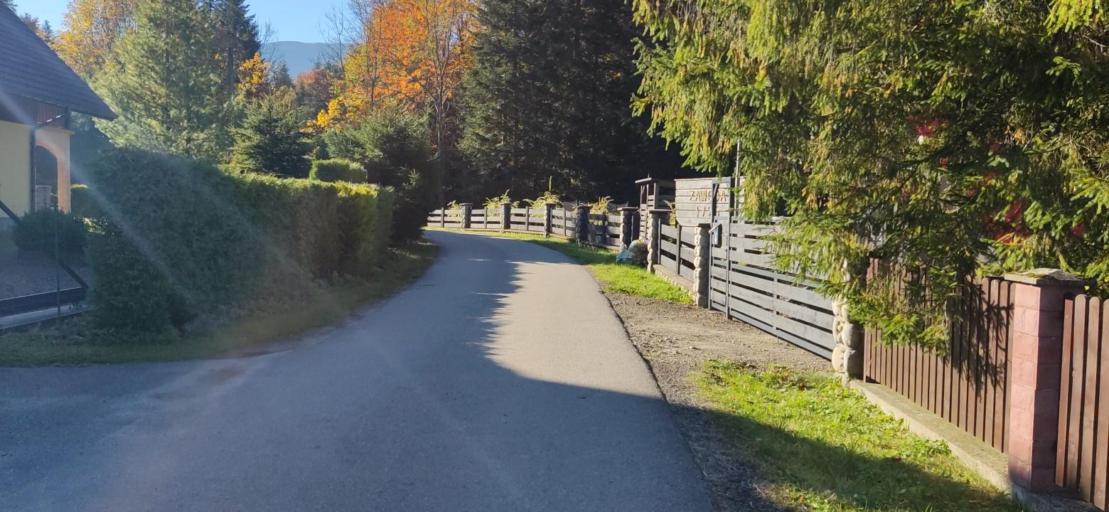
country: PL
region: Lesser Poland Voivodeship
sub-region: Powiat suski
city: Zawoja
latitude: 49.6196
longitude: 19.5402
